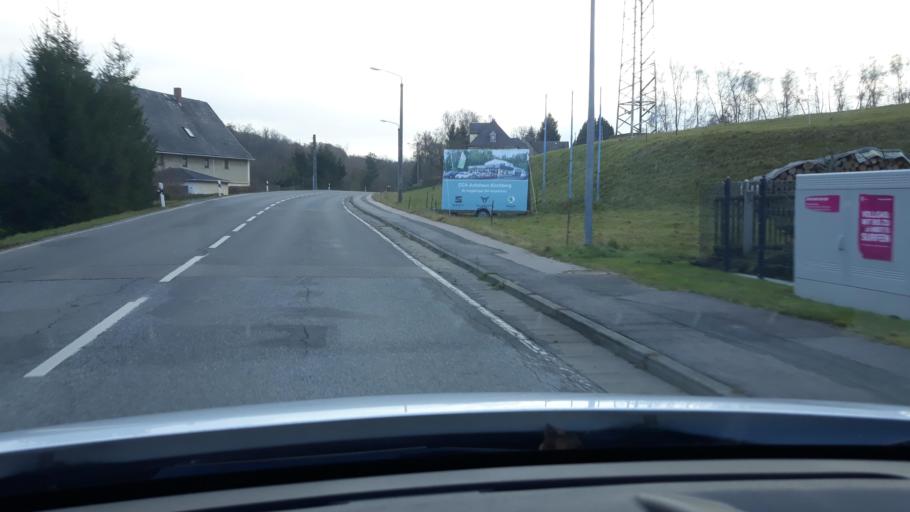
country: DE
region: Saxony
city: Kirchberg
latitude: 50.6357
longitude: 12.5187
